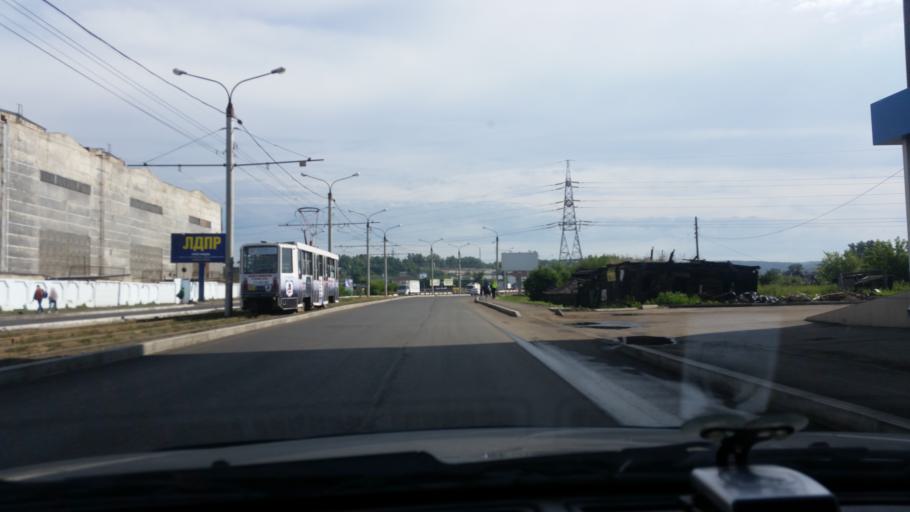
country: RU
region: Irkutsk
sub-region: Irkutskiy Rayon
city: Irkutsk
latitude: 52.2899
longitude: 104.3086
